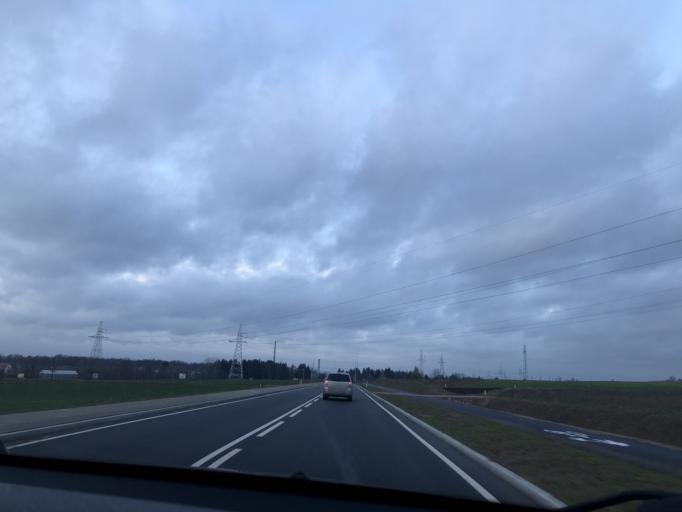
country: PL
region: Podlasie
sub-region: Lomza
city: Lomza
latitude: 53.1476
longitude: 22.0523
